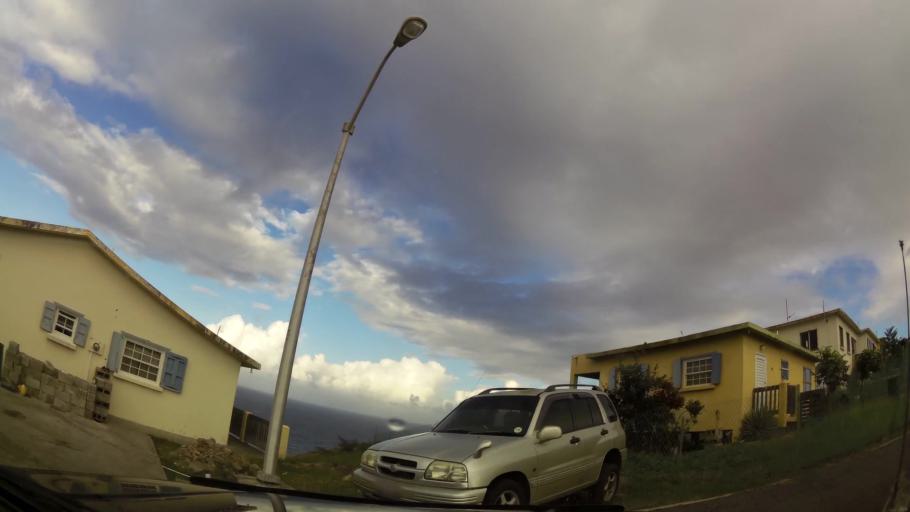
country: MS
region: Saint Peter
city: Brades
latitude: 16.7952
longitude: -62.1884
